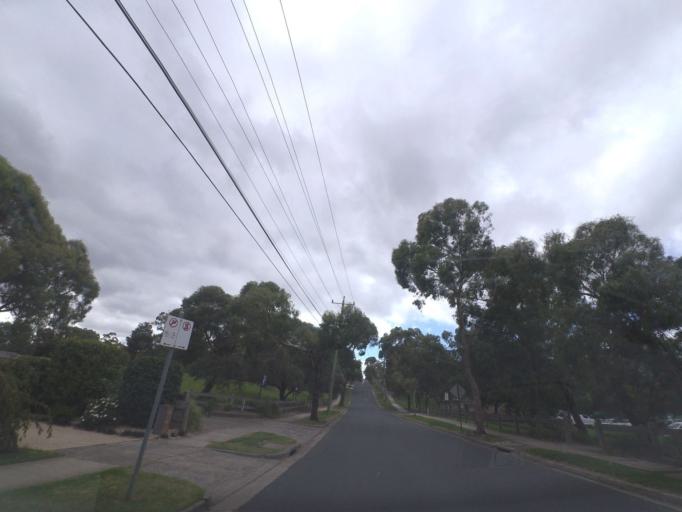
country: AU
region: Victoria
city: Mitcham
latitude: -37.8275
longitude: 145.2088
